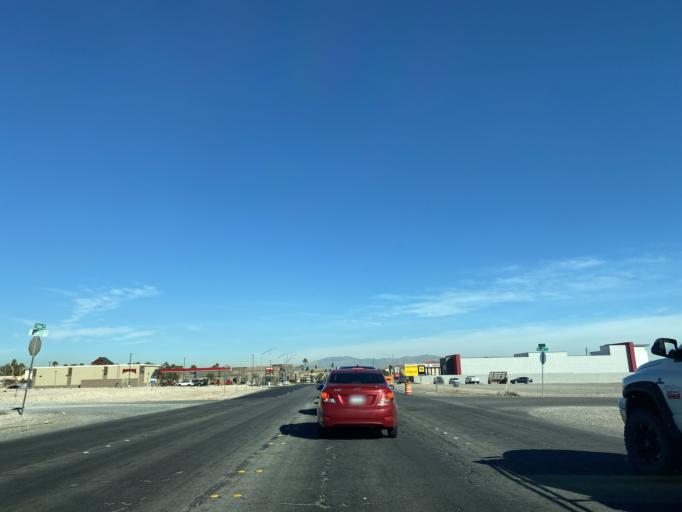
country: US
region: Nevada
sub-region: Clark County
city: Spring Valley
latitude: 36.0833
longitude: -115.2251
